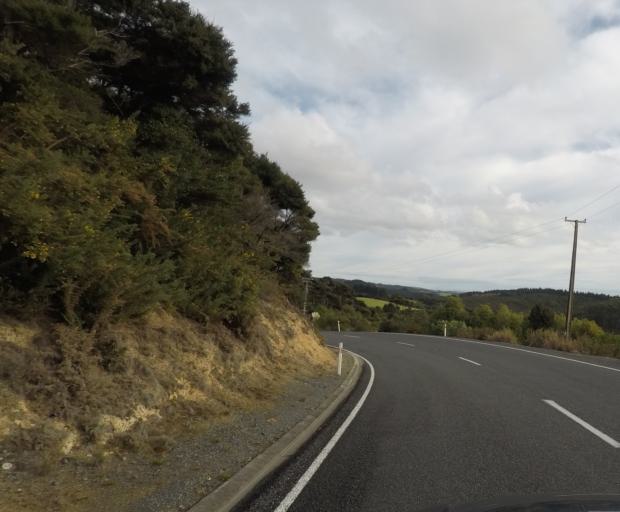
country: NZ
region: Northland
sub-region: Whangarei
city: Ruakaka
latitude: -36.0593
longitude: 174.5618
